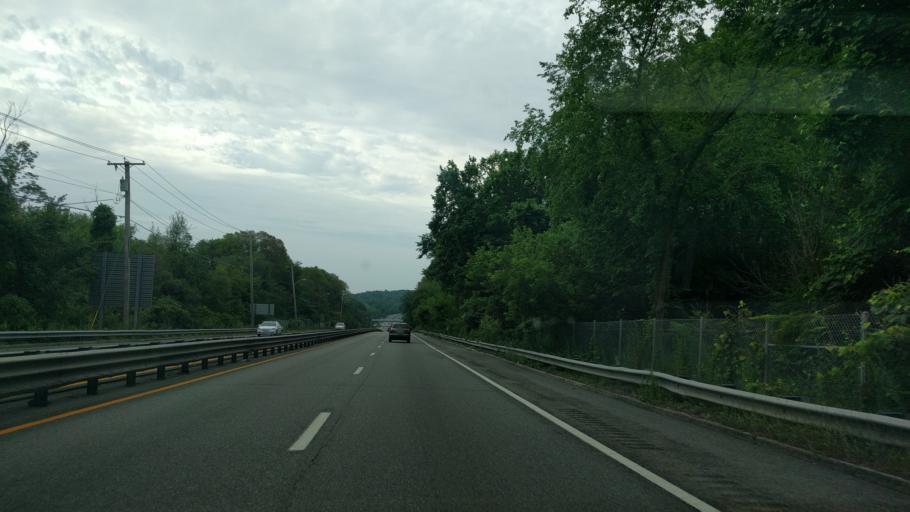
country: US
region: Rhode Island
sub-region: Providence County
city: Cumberland Hill
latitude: 41.9314
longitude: -71.4631
